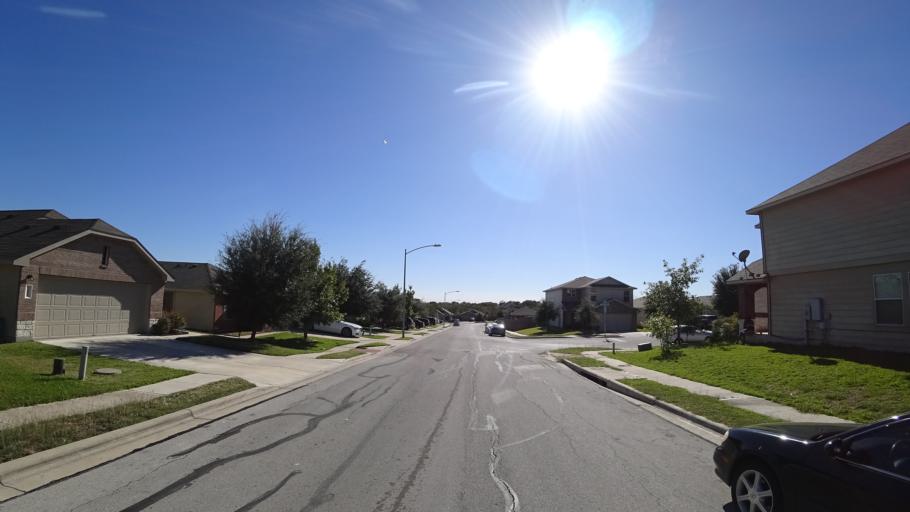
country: US
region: Texas
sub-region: Travis County
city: Hornsby Bend
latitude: 30.2797
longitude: -97.6275
